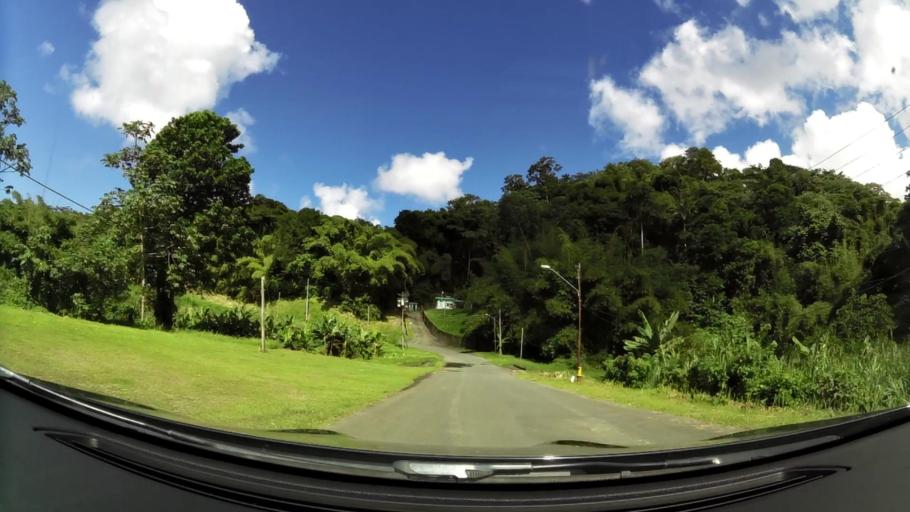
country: TT
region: Eastern Tobago
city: Roxborough
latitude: 11.3015
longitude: -60.6268
